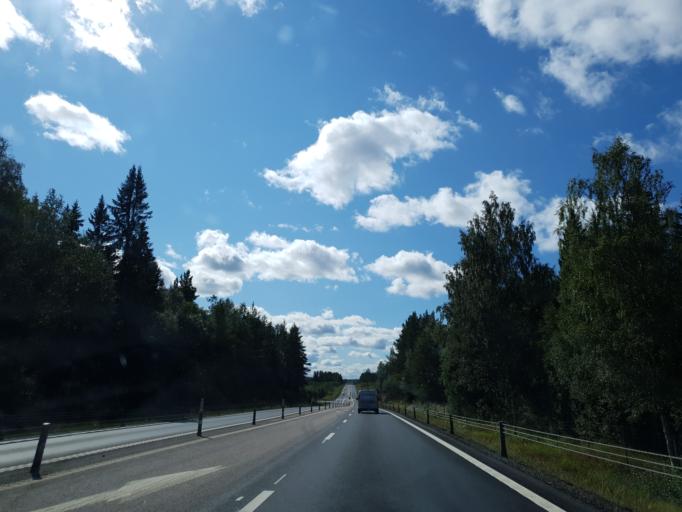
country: SE
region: Vaesterbotten
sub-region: Nordmalings Kommun
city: Nordmaling
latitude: 63.5136
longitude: 19.3610
